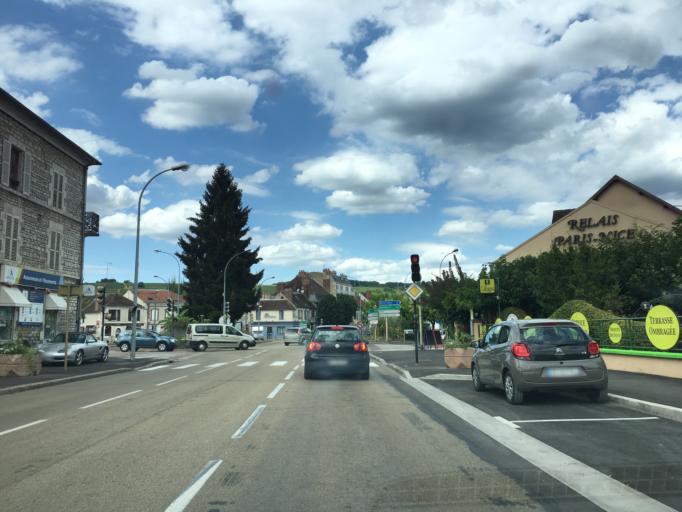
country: FR
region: Bourgogne
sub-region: Departement de l'Yonne
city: Joigny
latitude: 47.9764
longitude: 3.3944
